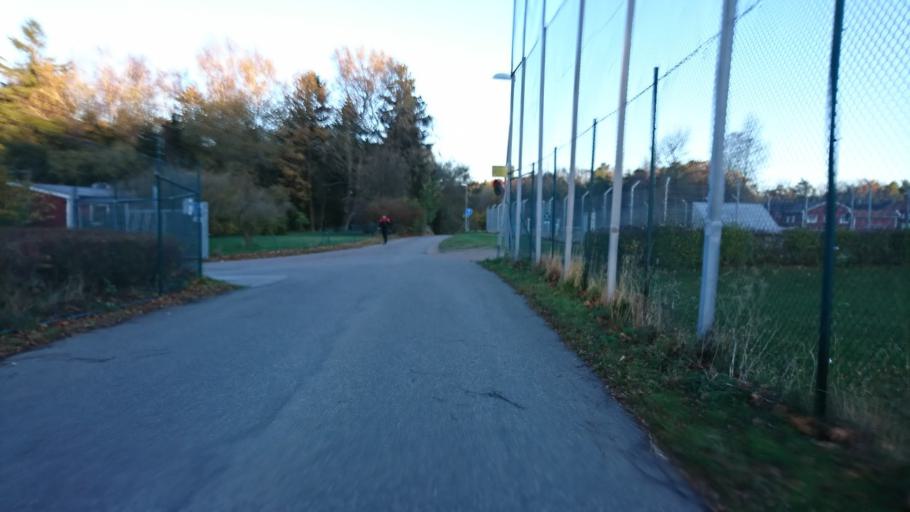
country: SE
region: Vaestra Goetaland
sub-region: Molndal
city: Moelndal
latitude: 57.6806
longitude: 12.0238
